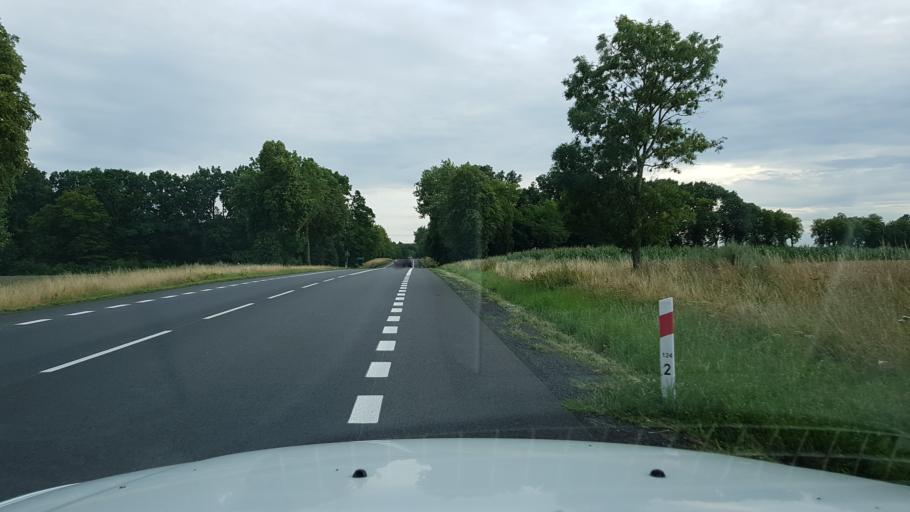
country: PL
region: West Pomeranian Voivodeship
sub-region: Powiat bialogardzki
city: Bialogard
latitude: 54.1007
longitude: 15.9952
